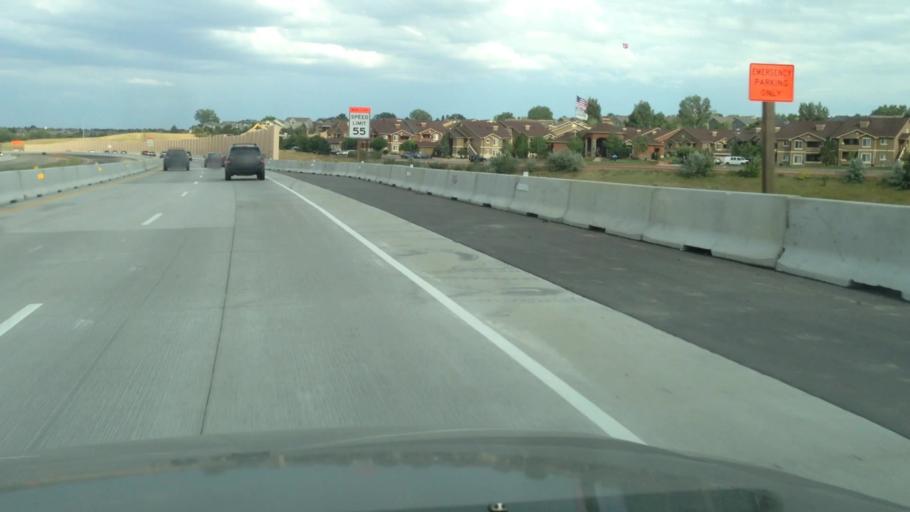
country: US
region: Colorado
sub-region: Arapahoe County
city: Southglenn
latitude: 39.5600
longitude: -104.9389
